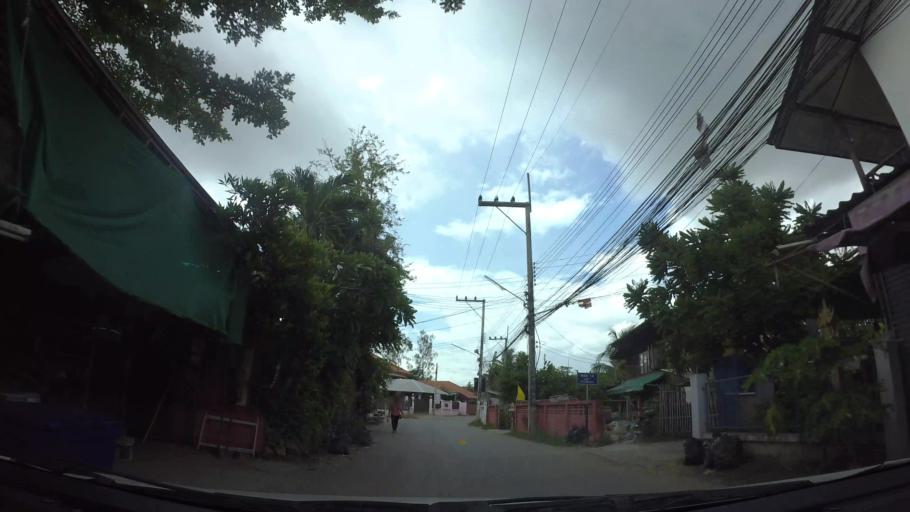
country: TH
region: Chiang Mai
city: Saraphi
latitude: 18.7494
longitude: 99.0390
